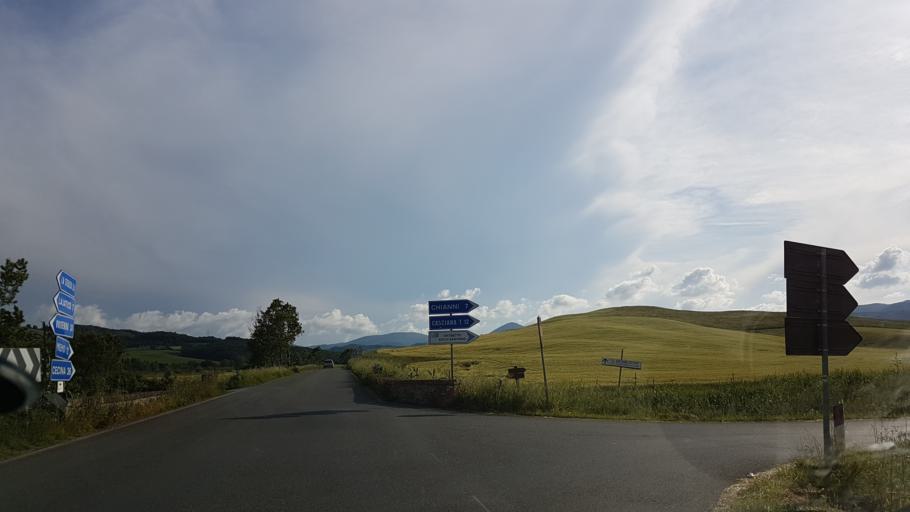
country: IT
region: Tuscany
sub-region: Province of Pisa
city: Lajatico
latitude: 43.4777
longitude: 10.6987
